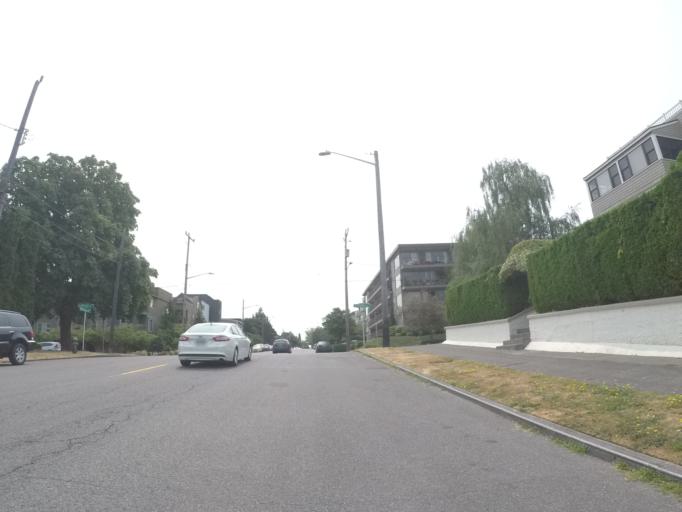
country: US
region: Washington
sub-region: King County
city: Seattle
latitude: 47.5909
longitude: -122.3862
